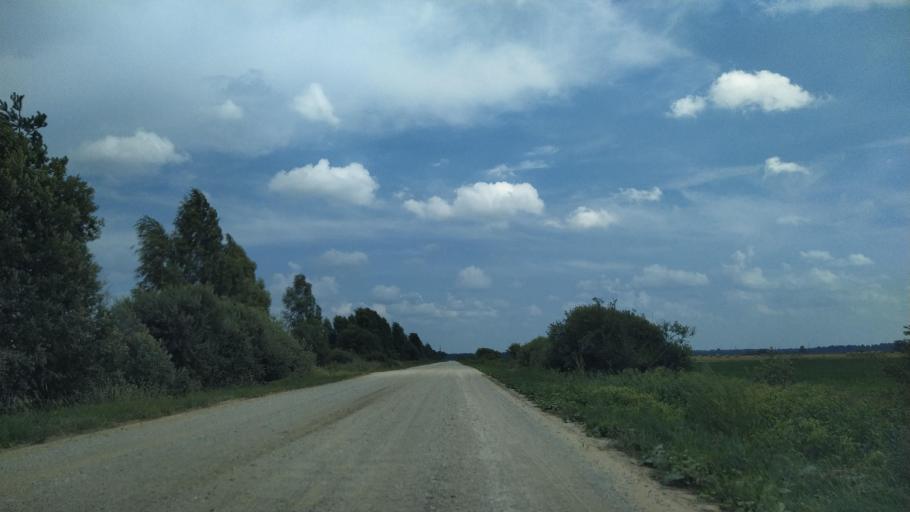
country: RU
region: Pskov
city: Pskov
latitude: 57.5851
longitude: 28.3270
